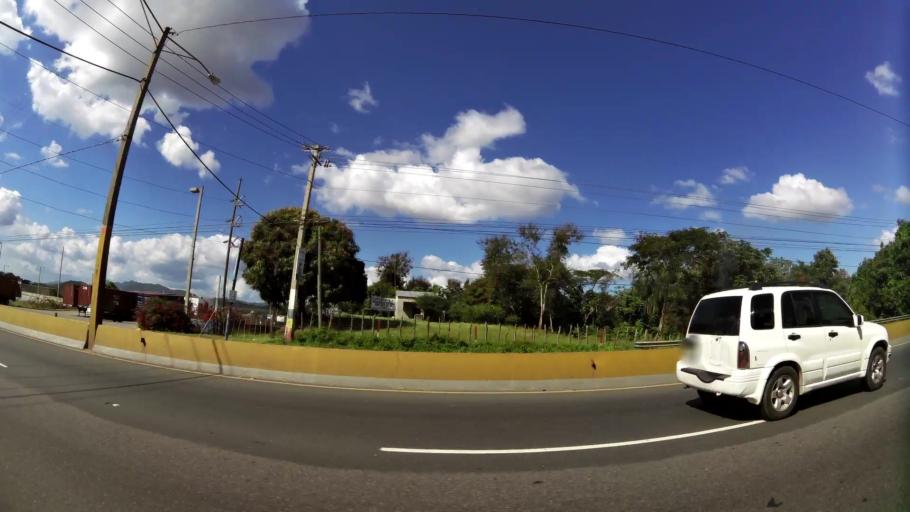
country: DO
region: Santo Domingo
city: Santo Domingo Oeste
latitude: 18.5610
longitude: -70.0633
